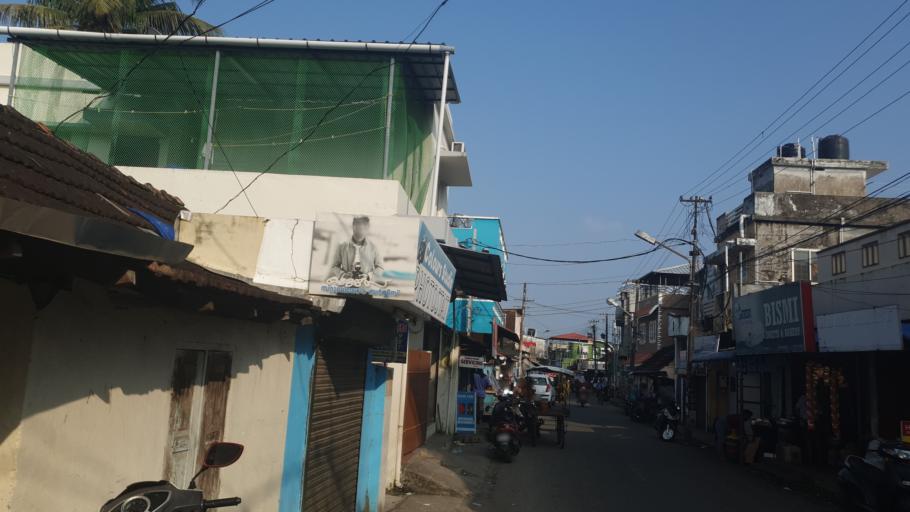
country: IN
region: Kerala
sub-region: Ernakulam
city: Cochin
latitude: 9.9630
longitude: 76.2515
